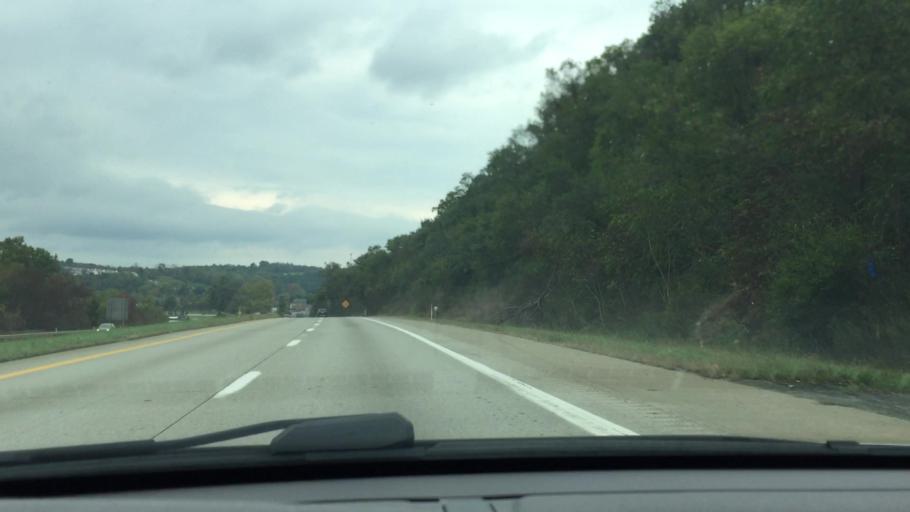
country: US
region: Pennsylvania
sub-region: Washington County
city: Canonsburg
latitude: 40.2699
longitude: -80.1598
